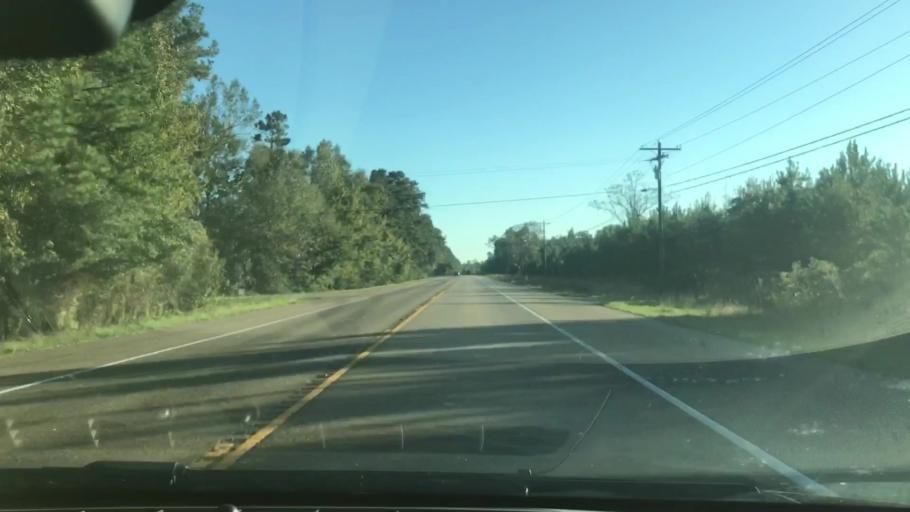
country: US
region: Louisiana
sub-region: Saint Tammany Parish
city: Abita Springs
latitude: 30.5721
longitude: -89.8714
